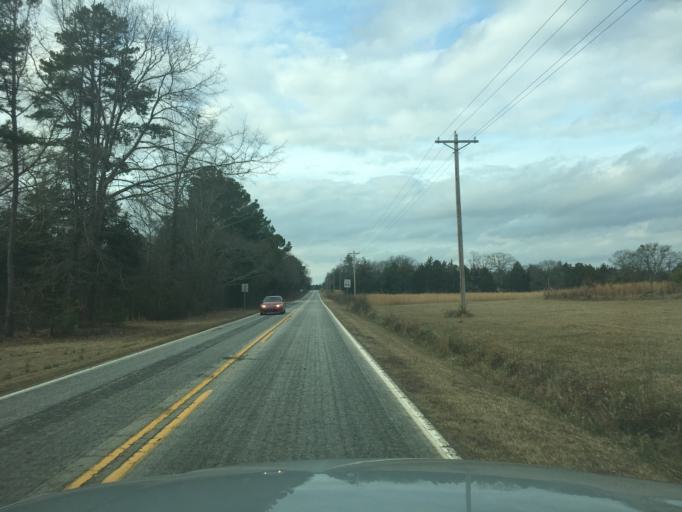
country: US
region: South Carolina
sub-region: Abbeville County
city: Due West
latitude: 34.3028
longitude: -82.4537
